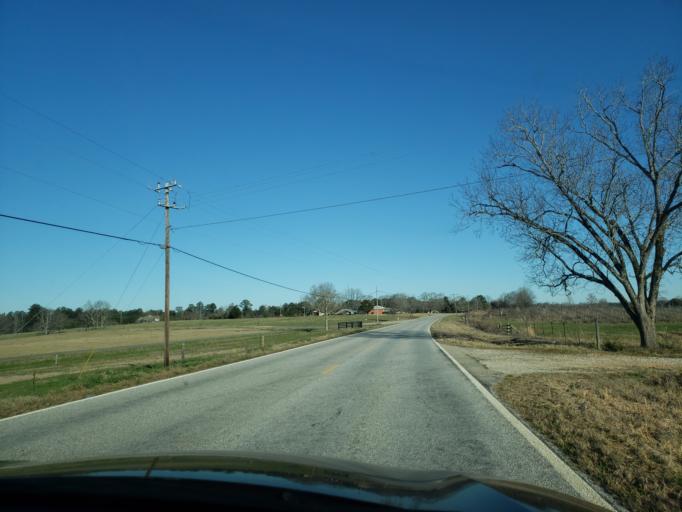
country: US
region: Alabama
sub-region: Elmore County
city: Tallassee
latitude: 32.5899
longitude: -85.7978
